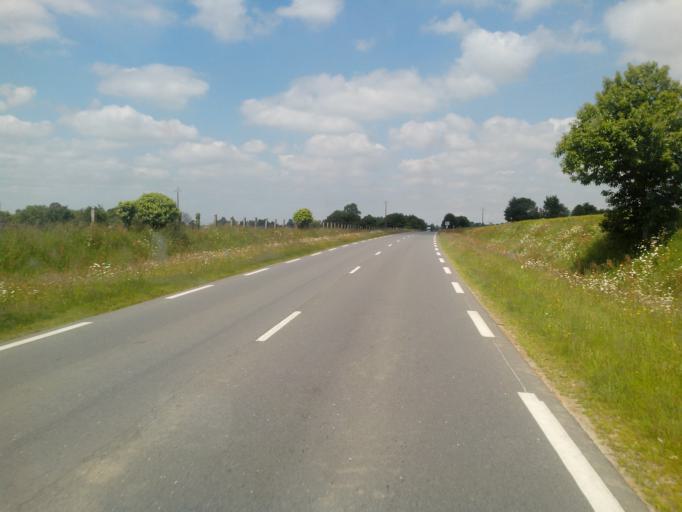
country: FR
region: Brittany
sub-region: Departement d'Ille-et-Vilaine
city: Saint-Germain-en-Cogles
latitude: 48.3829
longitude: -1.2685
